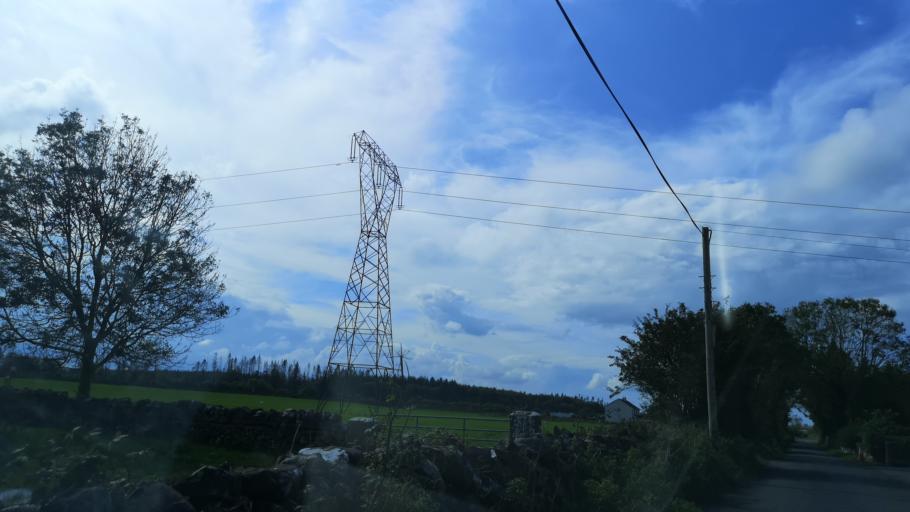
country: IE
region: Connaught
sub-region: County Galway
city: Athenry
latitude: 53.3004
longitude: -8.8202
